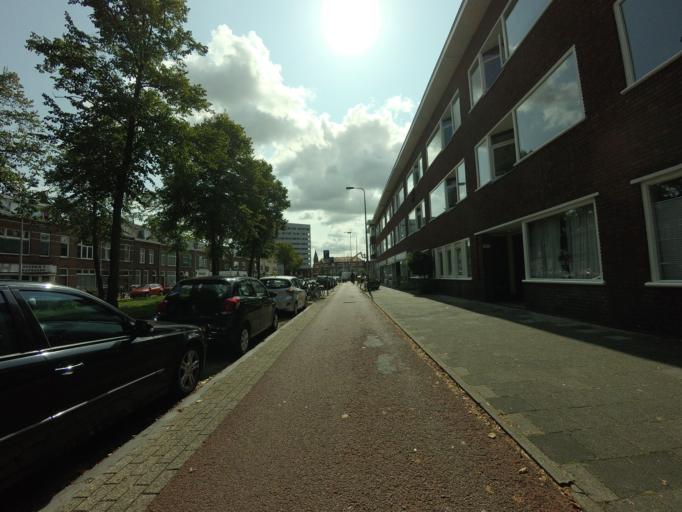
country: NL
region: Utrecht
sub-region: Gemeente Utrecht
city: Utrecht
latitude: 52.0791
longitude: 5.1140
